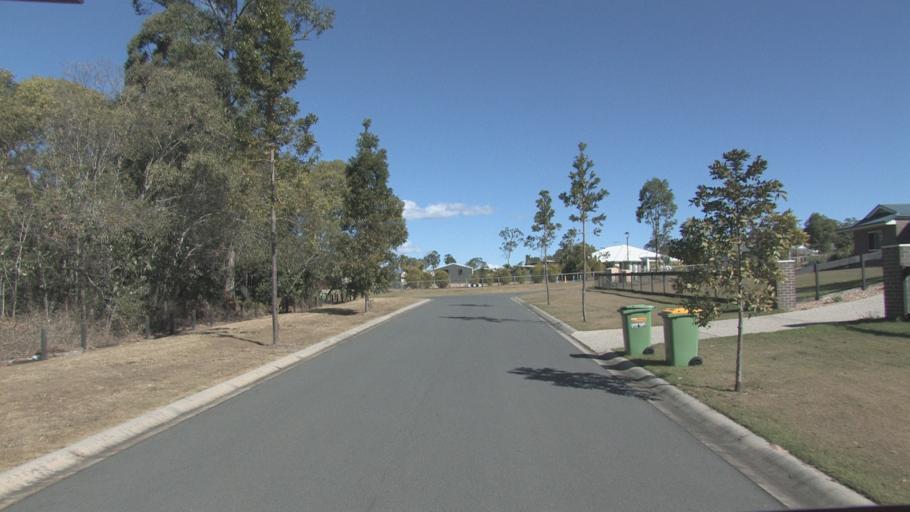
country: AU
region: Queensland
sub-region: Logan
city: North Maclean
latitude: -27.7564
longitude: 152.9491
